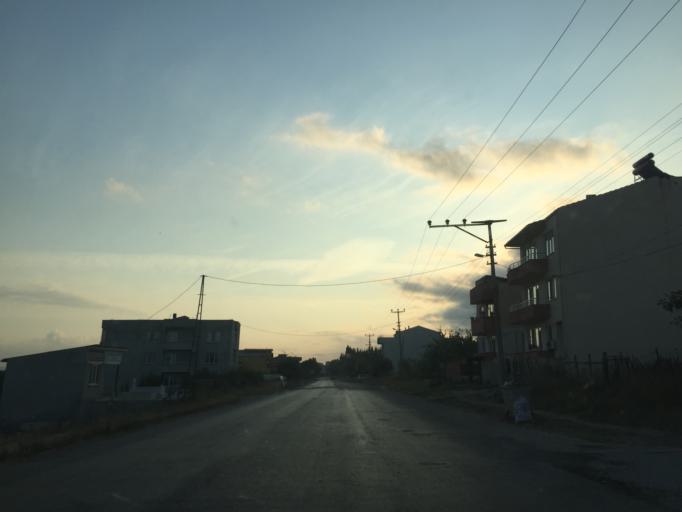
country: TR
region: Balikesir
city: Gonen
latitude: 40.0928
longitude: 27.6517
